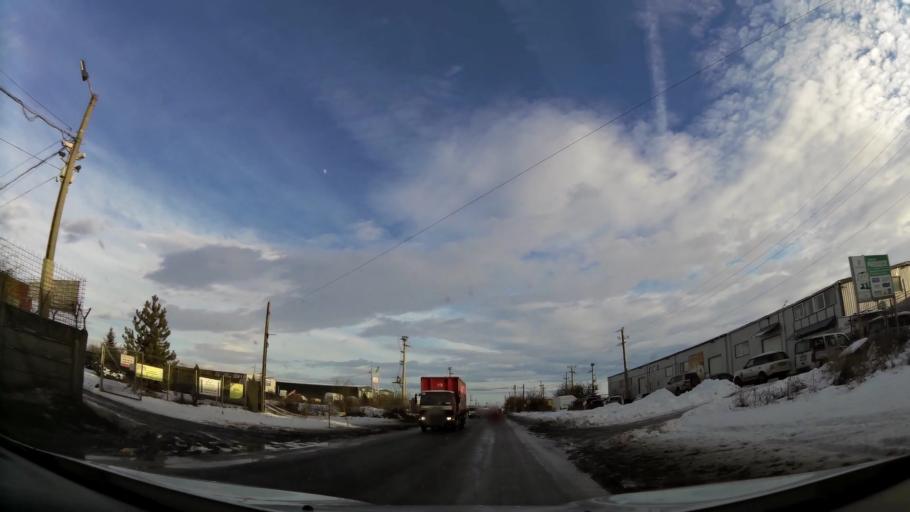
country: RO
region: Ilfov
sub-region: Comuna Jilava
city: Jilava
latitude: 44.3385
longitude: 26.0937
